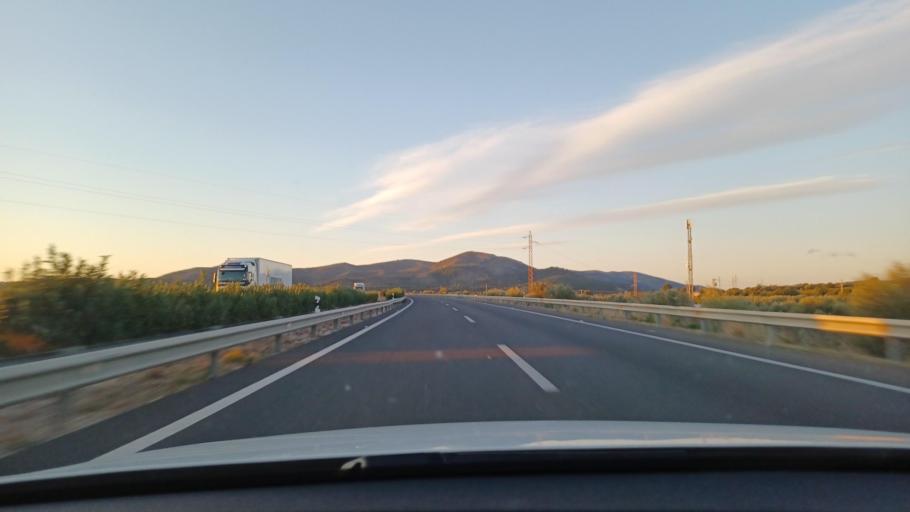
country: ES
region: Valencia
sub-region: Provincia de Castello
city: Calig
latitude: 40.4124
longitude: 0.3714
